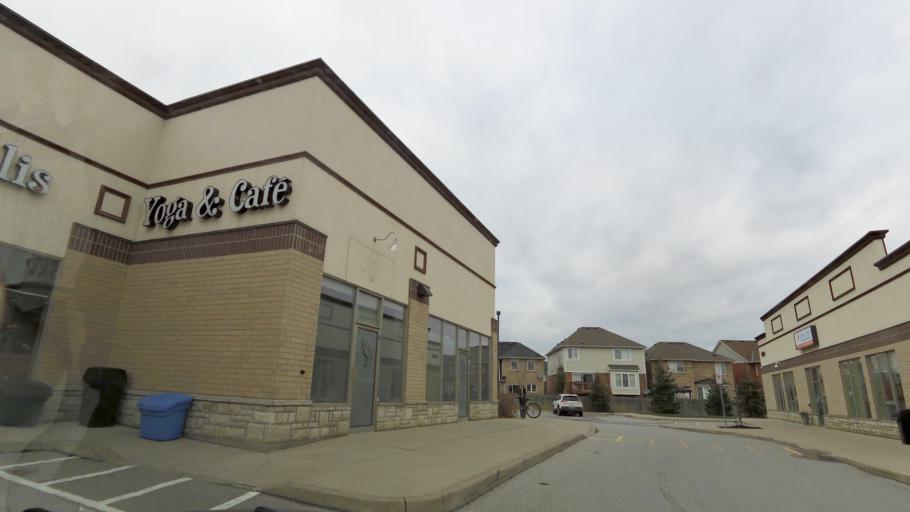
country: CA
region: Ontario
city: Burlington
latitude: 43.3967
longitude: -79.8286
